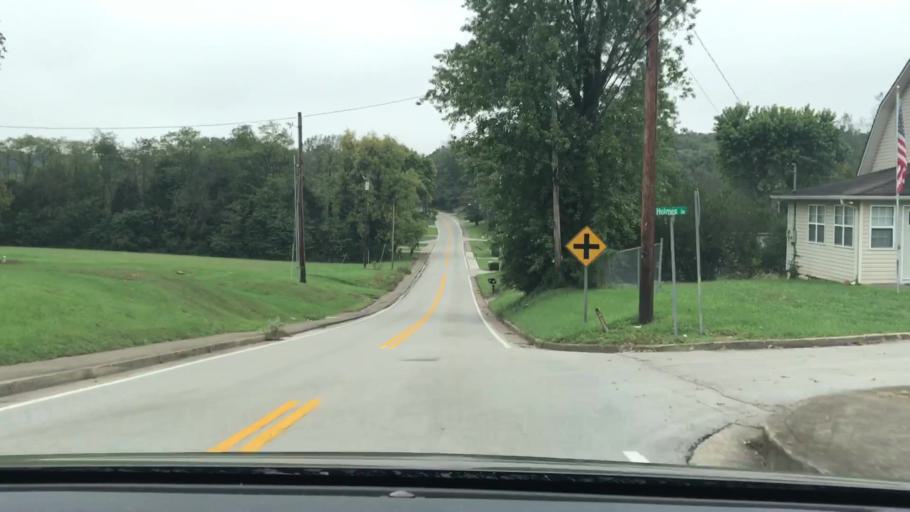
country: US
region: Kentucky
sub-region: Pulaski County
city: Somerset
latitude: 37.0931
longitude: -84.5935
